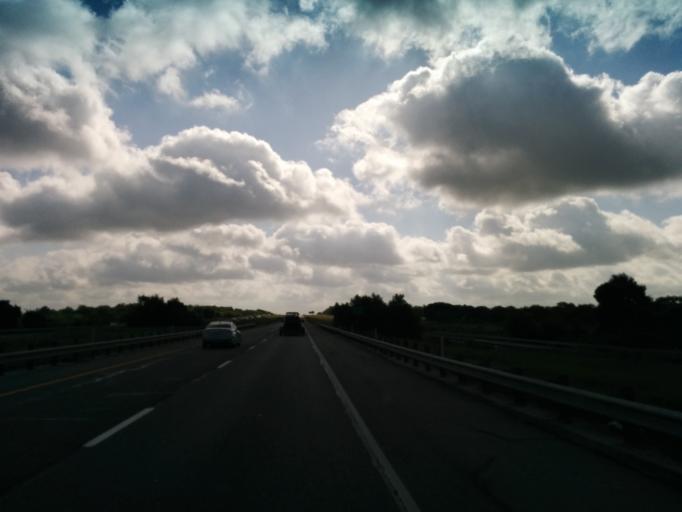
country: US
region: Texas
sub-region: Caldwell County
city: Luling
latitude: 29.6377
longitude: -97.7238
